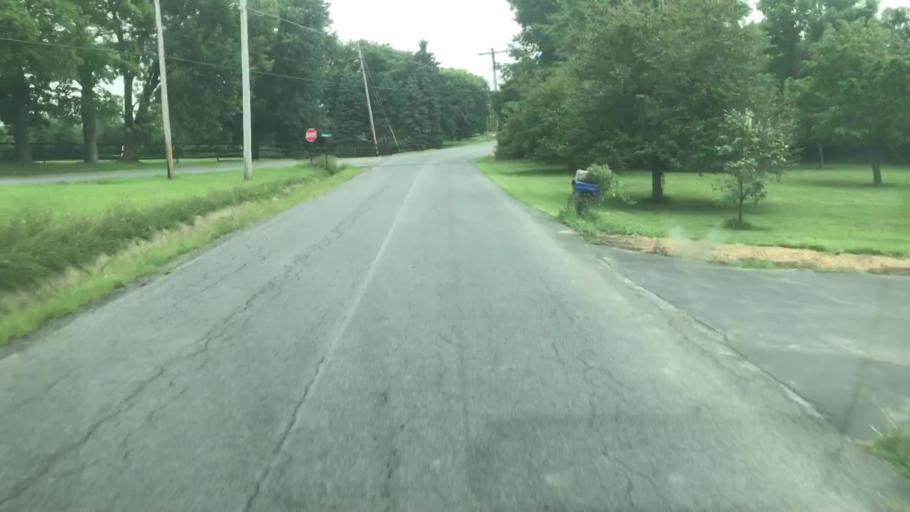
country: US
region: New York
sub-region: Onondaga County
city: Skaneateles
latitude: 42.9558
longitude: -76.4557
